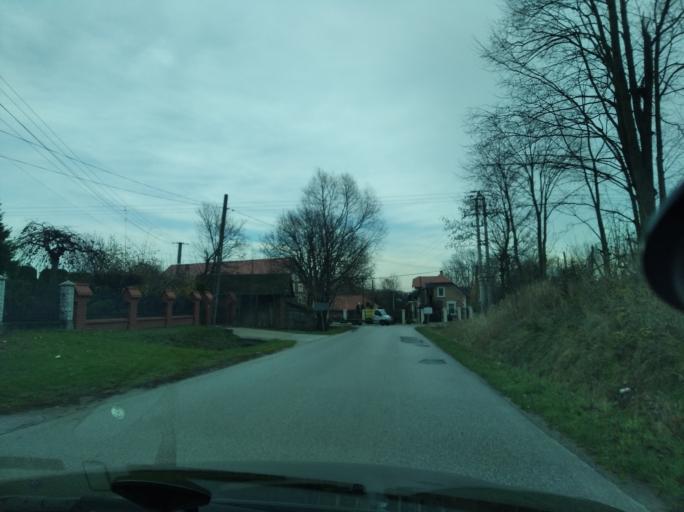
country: PL
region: Subcarpathian Voivodeship
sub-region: Powiat lancucki
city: Albigowa
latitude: 50.0345
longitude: 22.2276
